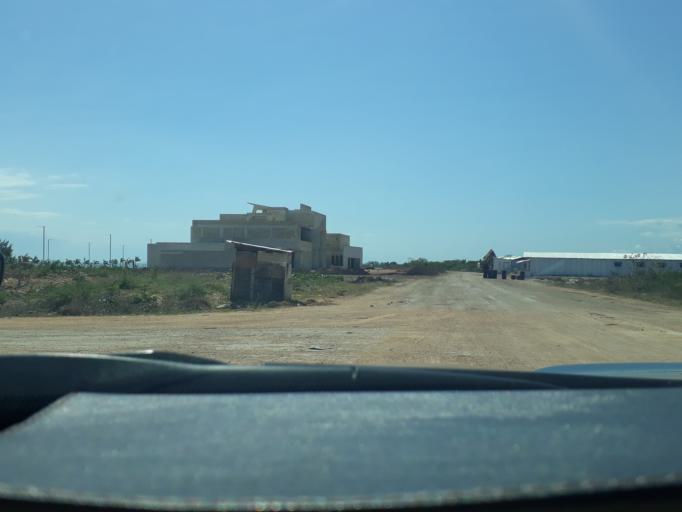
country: TZ
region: Zanzibar Urban/West
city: Zanzibar
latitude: -6.3024
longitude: 39.2639
